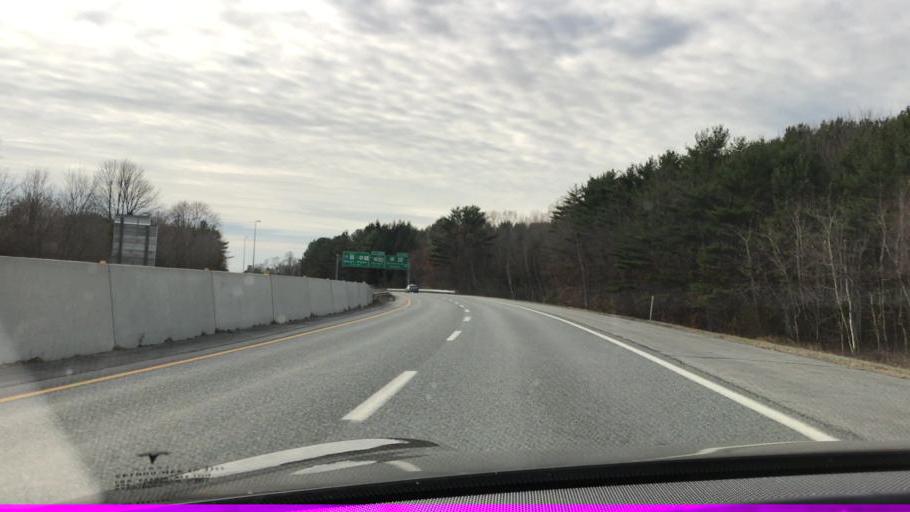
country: US
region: Maine
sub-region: Penobscot County
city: Bangor
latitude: 44.8037
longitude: -68.7996
